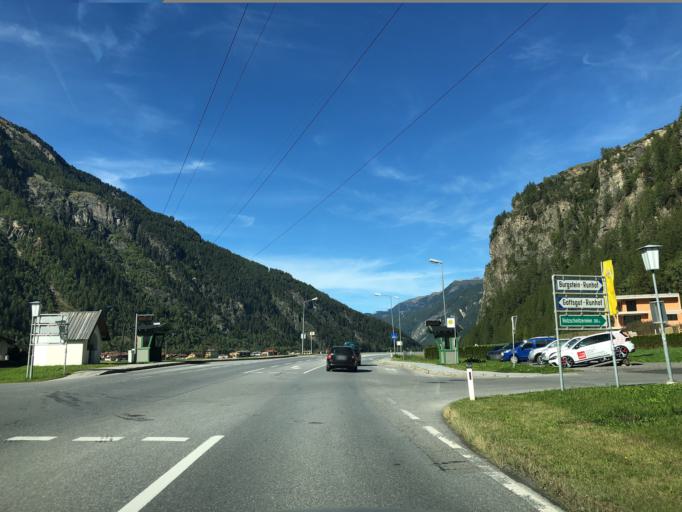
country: AT
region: Tyrol
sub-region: Politischer Bezirk Imst
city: Umhausen
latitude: 47.0501
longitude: 10.9663
